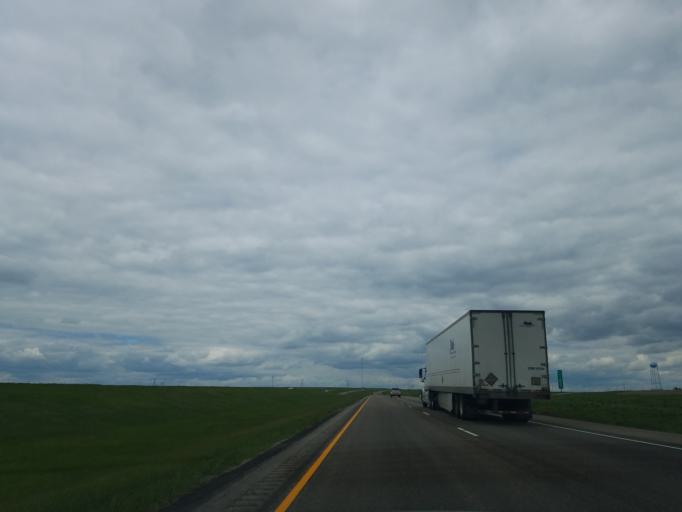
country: US
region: North Dakota
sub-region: Kidder County
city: Steele
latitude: 46.8477
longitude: -100.2421
